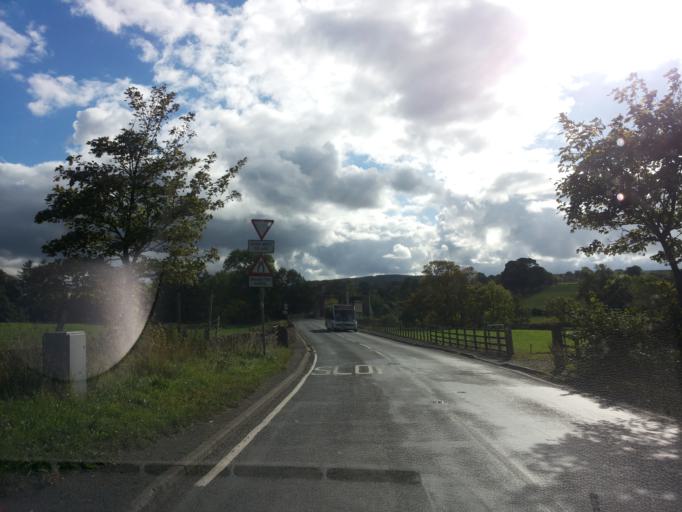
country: GB
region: England
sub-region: North Yorkshire
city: Leyburn
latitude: 54.2957
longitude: -1.8198
